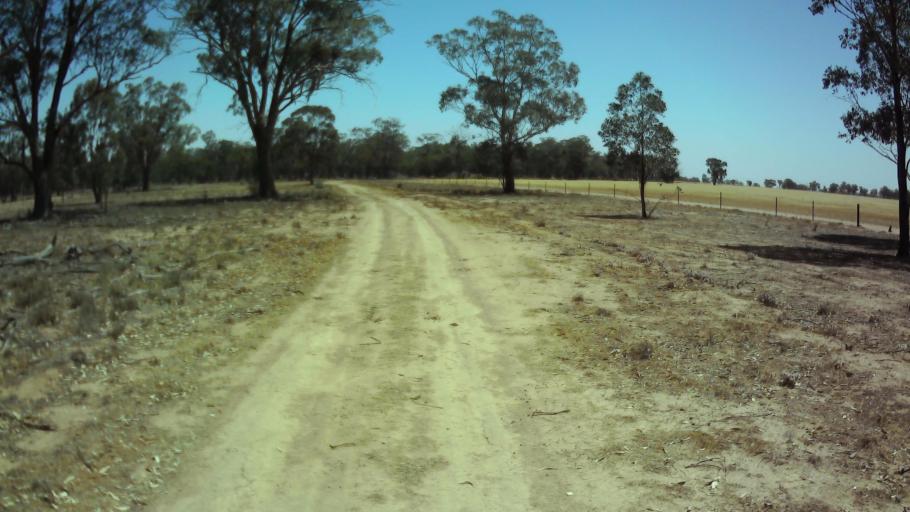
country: AU
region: New South Wales
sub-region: Weddin
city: Grenfell
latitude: -34.0691
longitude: 147.7937
